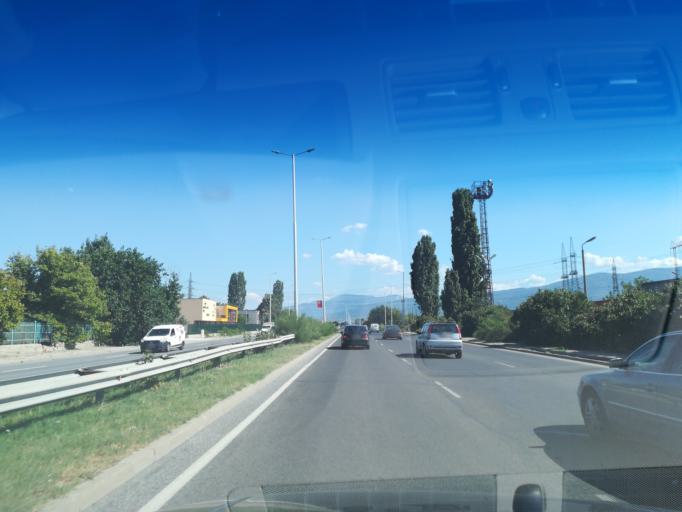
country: BG
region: Plovdiv
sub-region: Obshtina Plovdiv
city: Plovdiv
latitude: 42.1088
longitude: 24.7819
